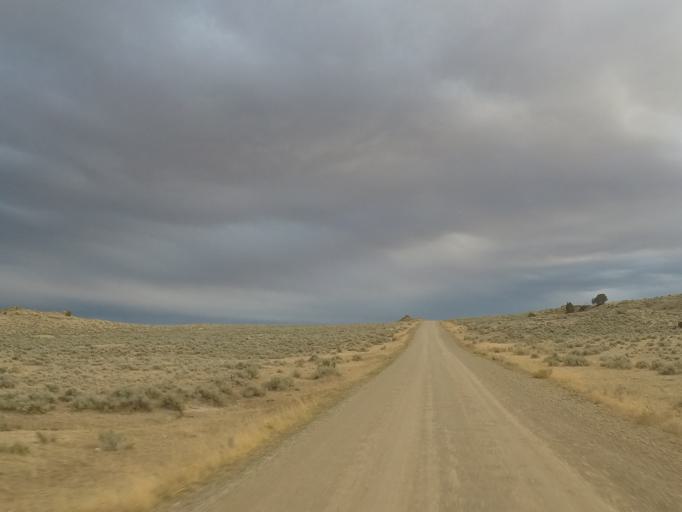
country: US
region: Montana
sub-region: Golden Valley County
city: Ryegate
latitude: 46.4261
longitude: -109.2509
